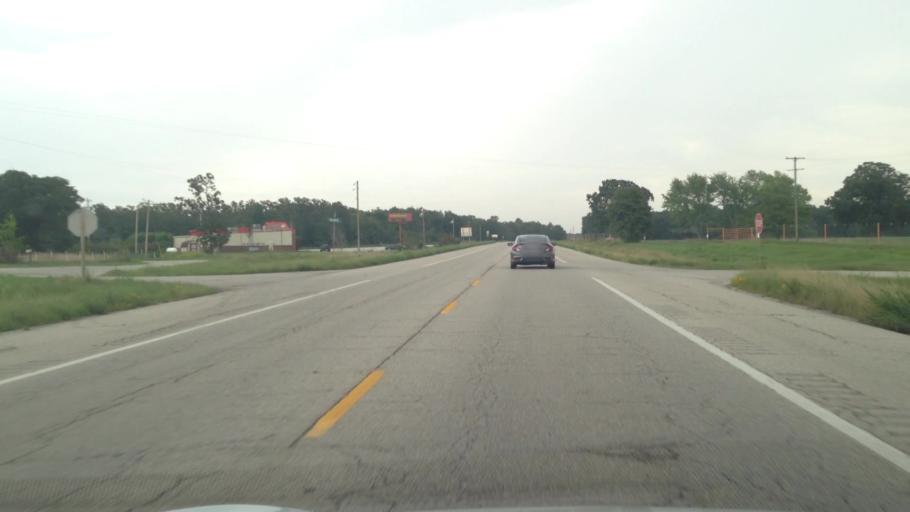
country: US
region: Kansas
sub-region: Cherokee County
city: Galena
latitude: 37.0095
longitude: -94.6241
